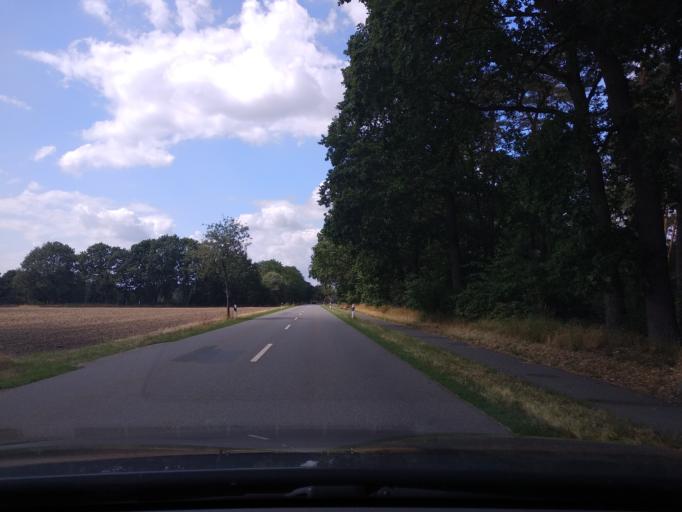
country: DE
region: Lower Saxony
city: Wagenhoff
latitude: 52.5092
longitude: 10.5026
